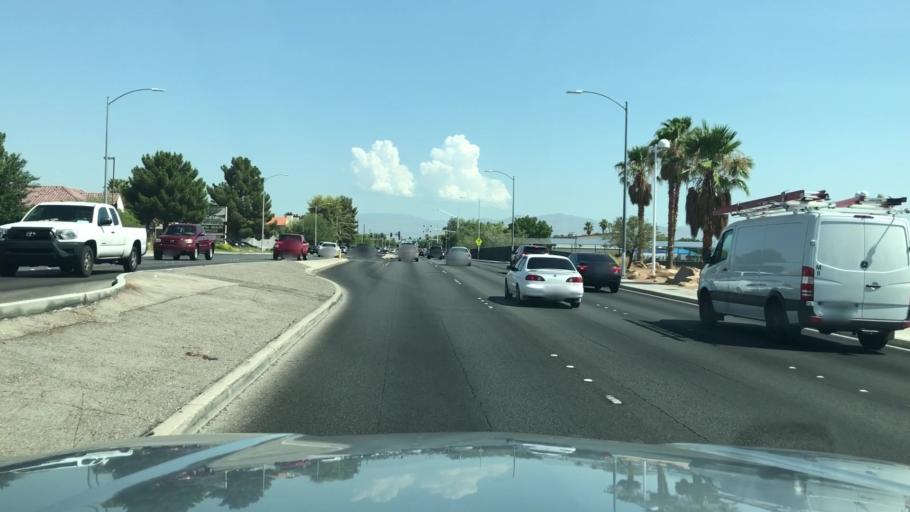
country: US
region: Nevada
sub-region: Clark County
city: Spring Valley
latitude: 36.1493
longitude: -115.2254
